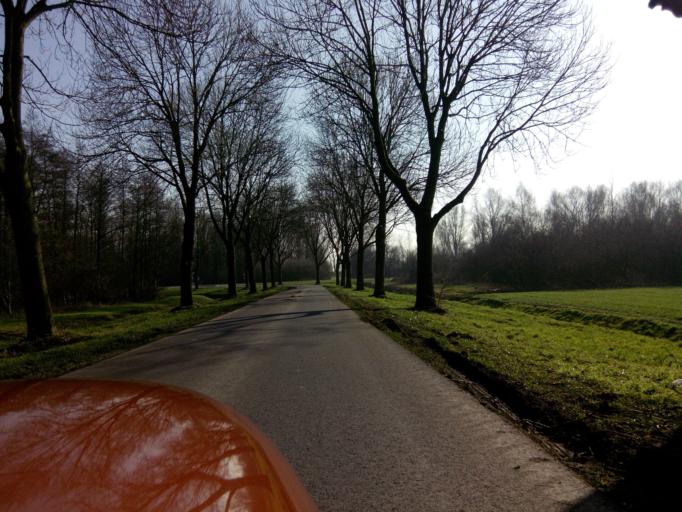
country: NL
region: Gelderland
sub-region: Gemeente Nijkerk
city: Nijkerk
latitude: 52.2689
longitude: 5.4817
